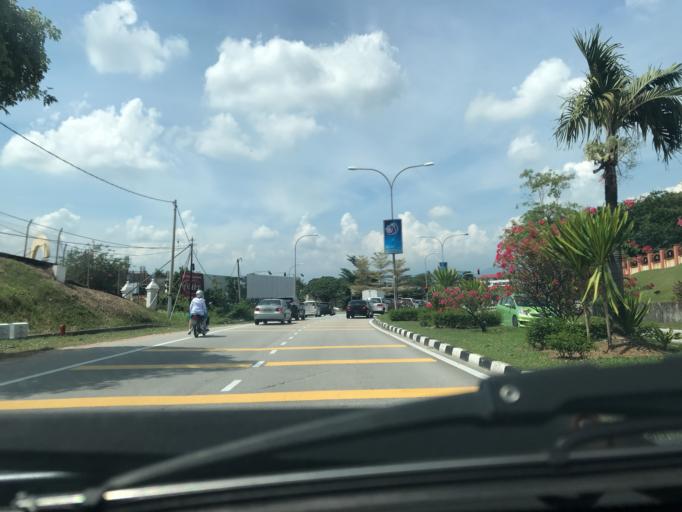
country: MY
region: Perak
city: Ipoh
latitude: 4.6017
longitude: 101.1009
